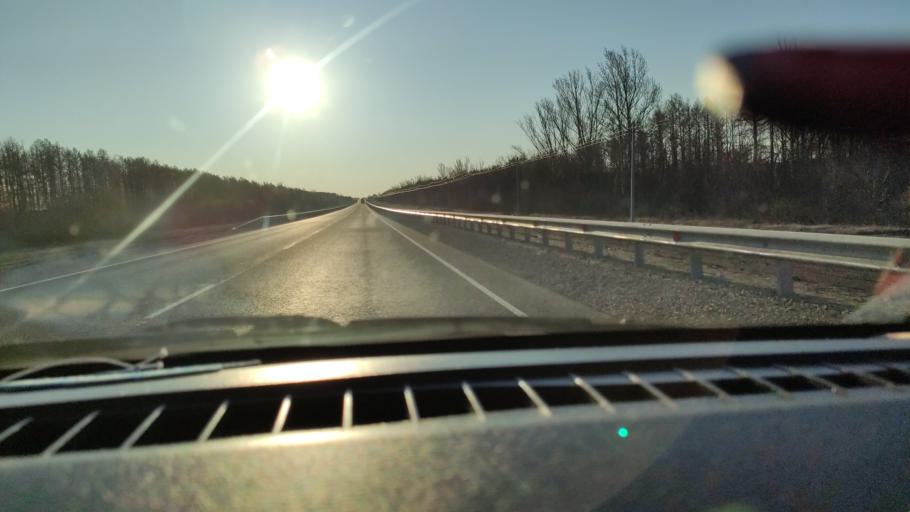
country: RU
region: Saratov
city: Shikhany
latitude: 52.1612
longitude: 47.1362
